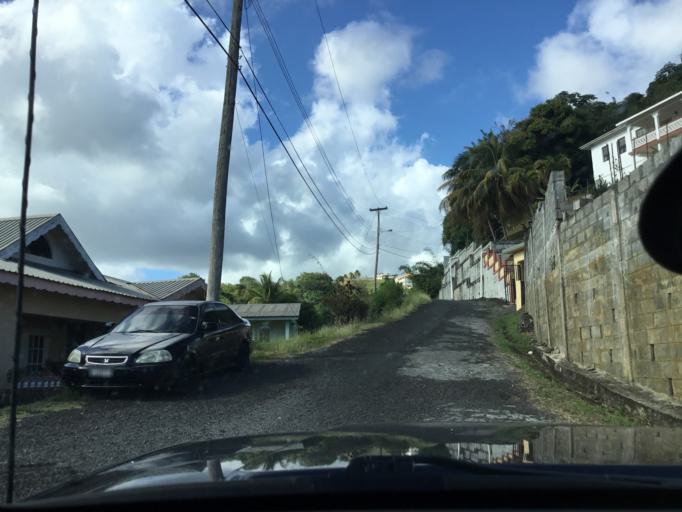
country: VC
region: Saint George
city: Kingstown
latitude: 13.1472
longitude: -61.1791
